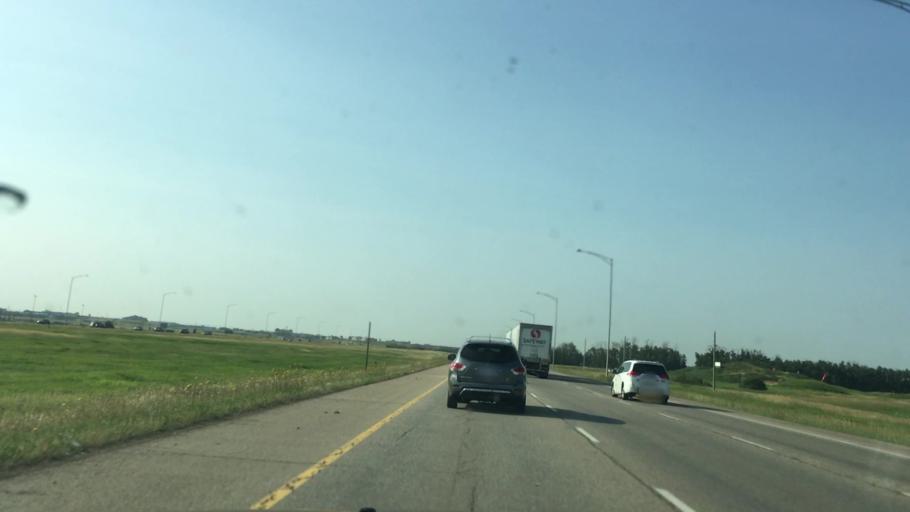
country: CA
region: Alberta
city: Leduc
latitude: 53.3281
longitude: -113.5499
